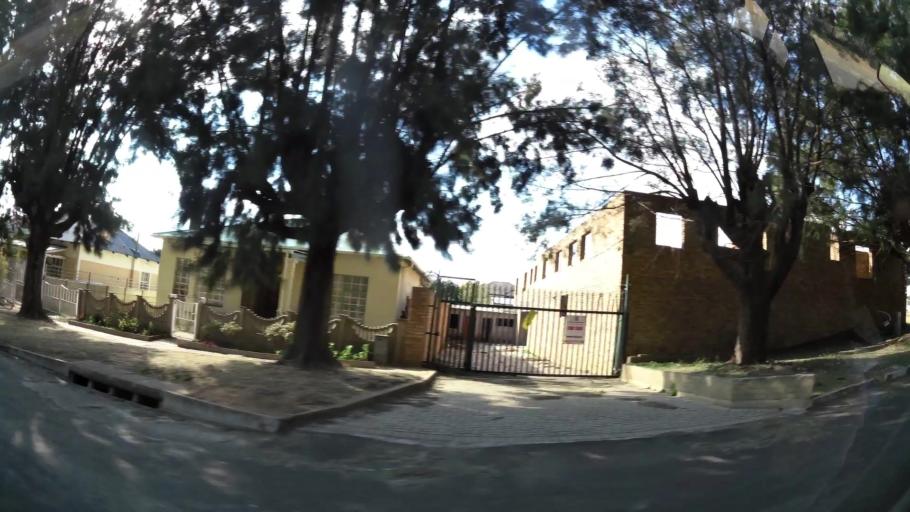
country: ZA
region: Gauteng
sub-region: West Rand District Municipality
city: Krugersdorp
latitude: -26.1033
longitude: 27.7663
